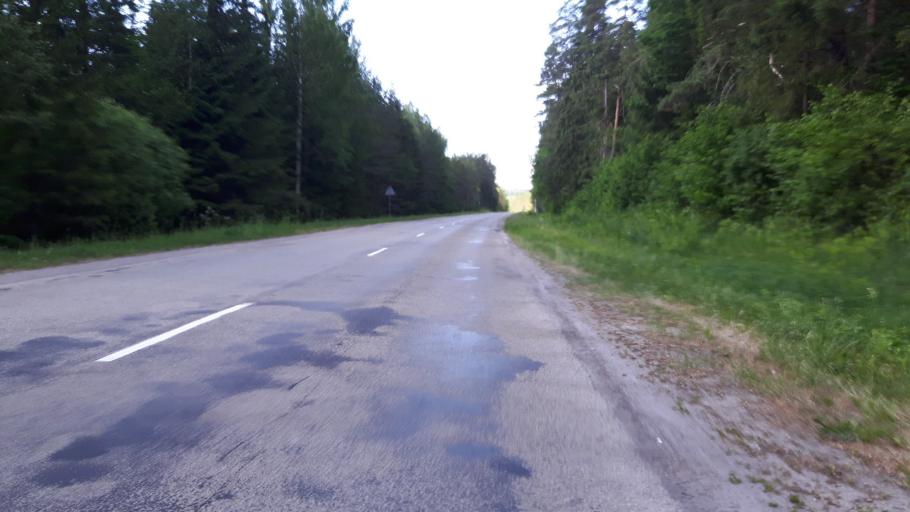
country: LV
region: Talsu Rajons
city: Sabile
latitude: 57.0725
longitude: 22.5340
